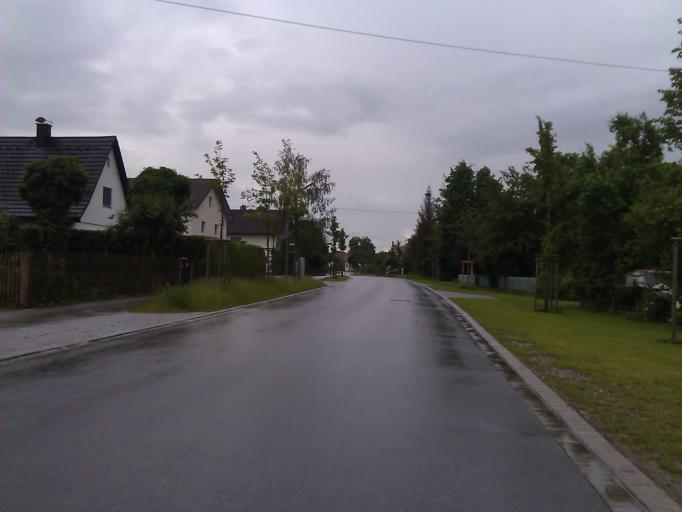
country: DE
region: Bavaria
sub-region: Swabia
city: Tussenhausen
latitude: 48.0616
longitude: 10.5839
